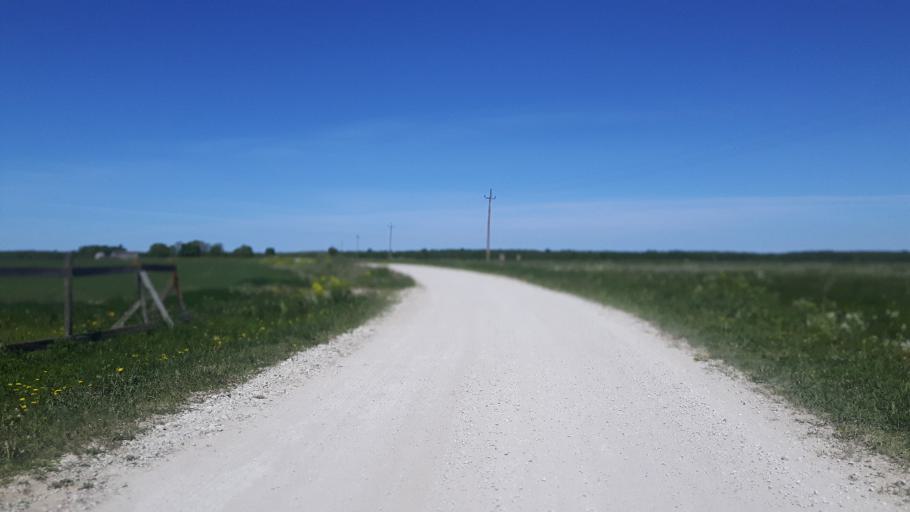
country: EE
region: Ida-Virumaa
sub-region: Toila vald
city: Voka
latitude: 59.3956
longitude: 27.6685
